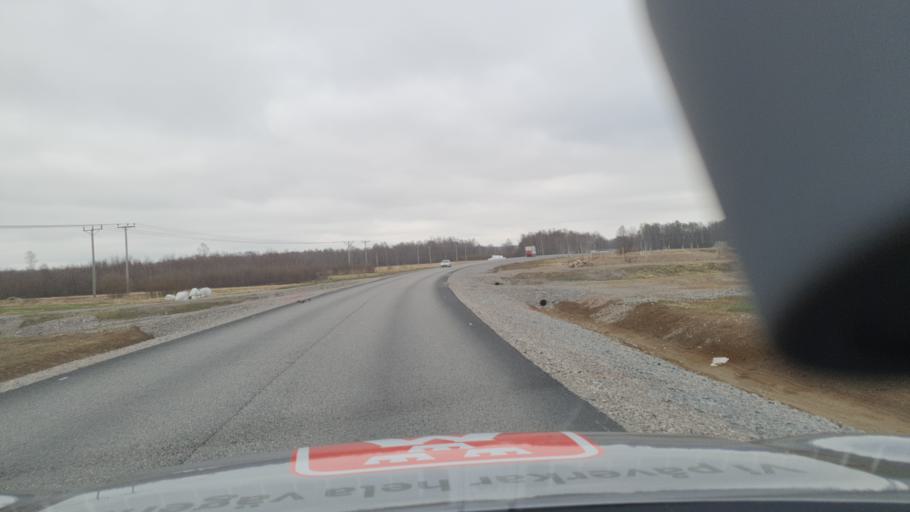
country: SE
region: Norrbotten
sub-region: Kalix Kommun
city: Rolfs
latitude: 65.8832
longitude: 23.0588
